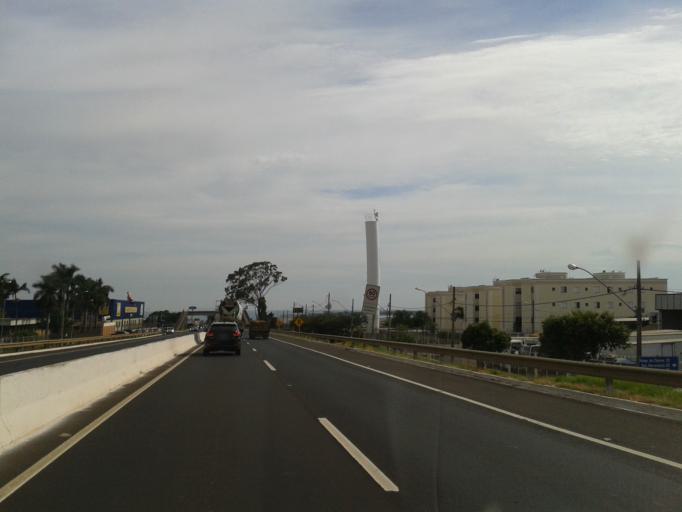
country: BR
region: Minas Gerais
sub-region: Uberlandia
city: Uberlandia
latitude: -18.8785
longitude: -48.2615
